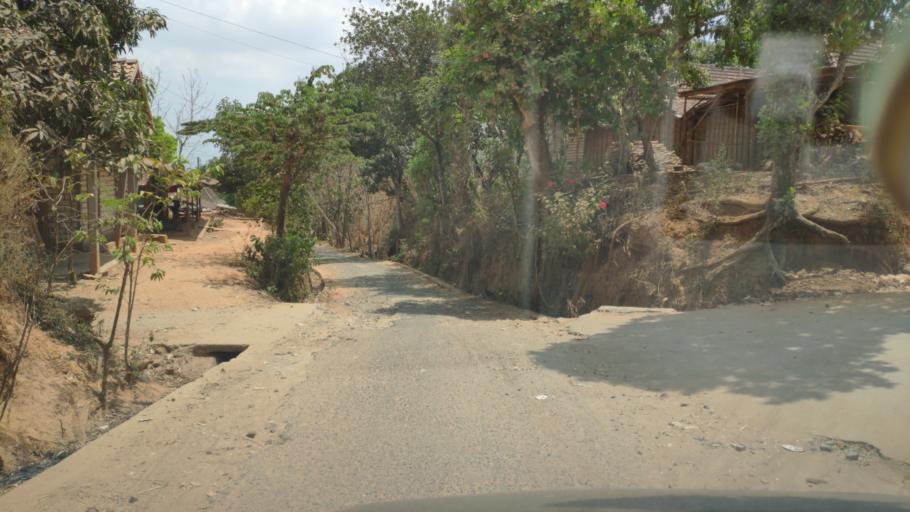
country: ID
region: Central Java
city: Kalinanas
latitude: -6.8633
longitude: 111.2513
